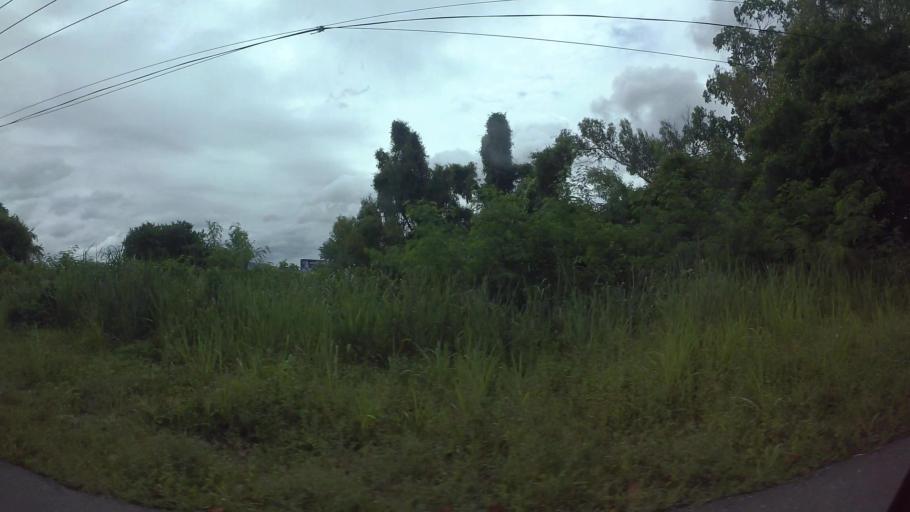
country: TH
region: Chon Buri
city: Si Racha
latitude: 13.1931
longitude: 100.9957
